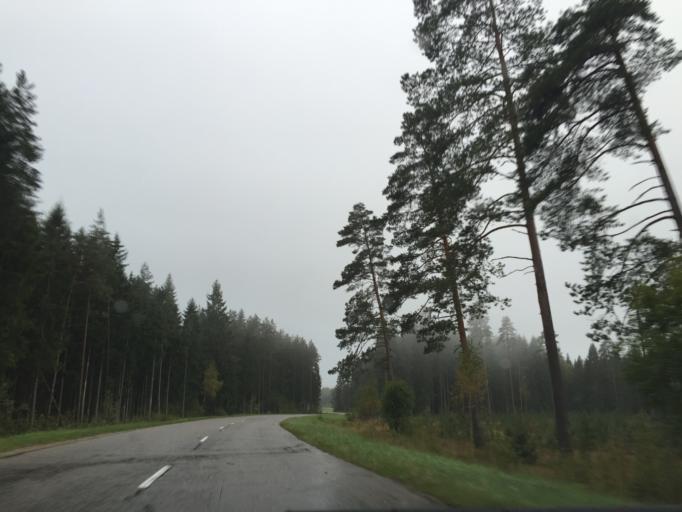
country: LV
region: Incukalns
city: Incukalns
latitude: 57.0815
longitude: 24.6727
